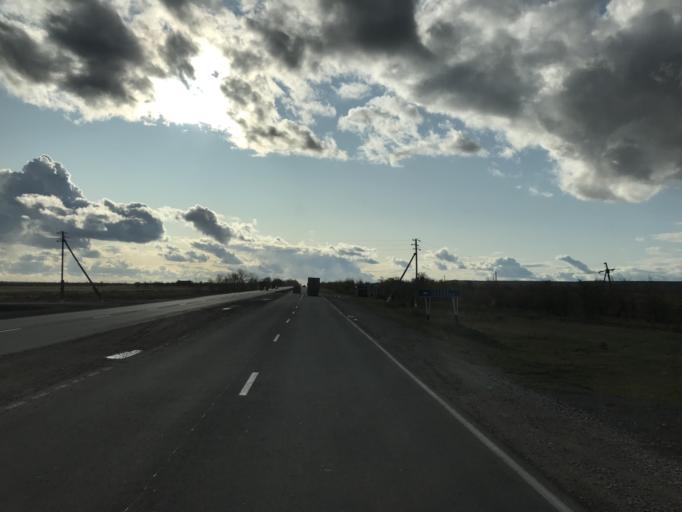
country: KZ
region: Qostanay
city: Rudnyy
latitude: 53.0125
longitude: 63.3074
